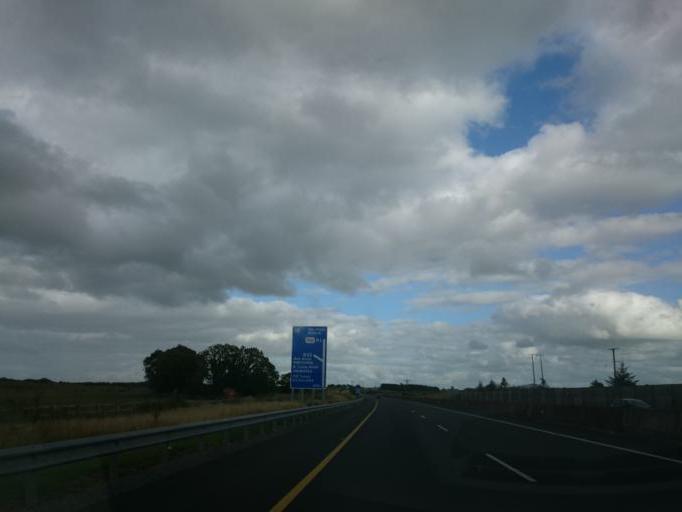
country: IE
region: Connaught
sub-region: County Galway
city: Loughrea
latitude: 53.2655
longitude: -8.6279
